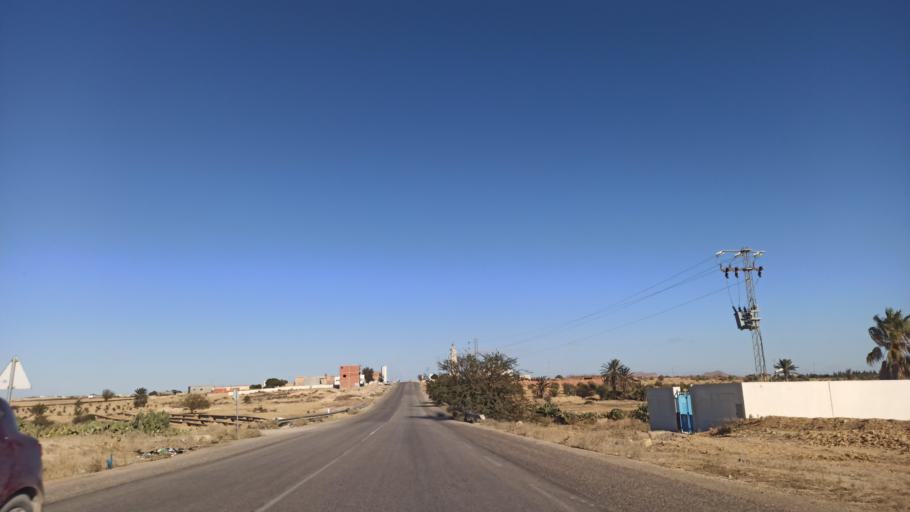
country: TN
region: Sidi Bu Zayd
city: Jilma
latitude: 35.2570
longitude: 9.4013
